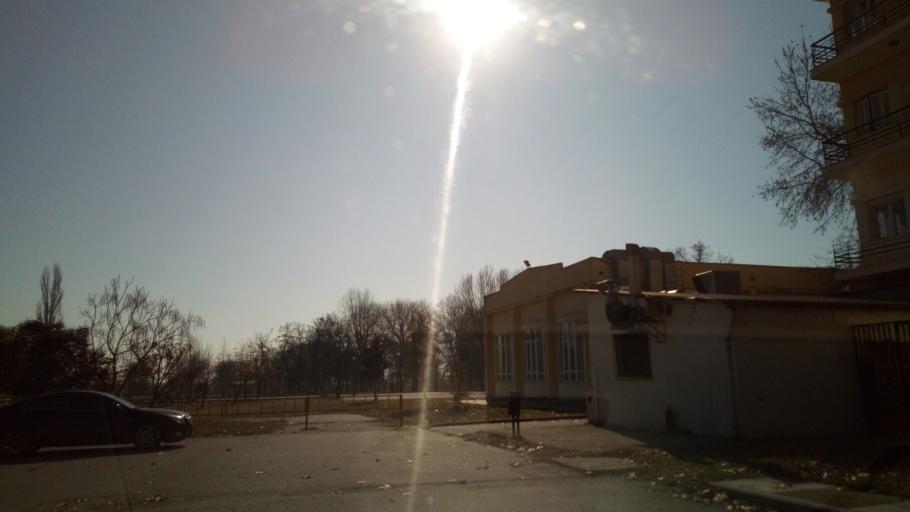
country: GR
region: Central Macedonia
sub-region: Nomos Thessalonikis
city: Lagkadas
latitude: 40.7333
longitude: 23.0862
